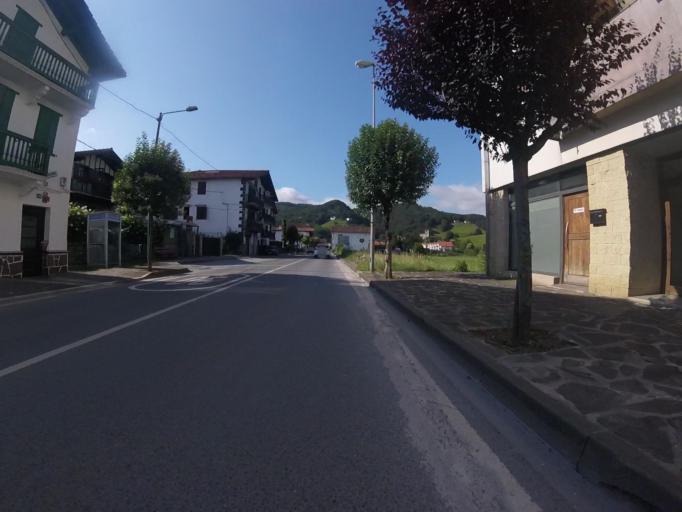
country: ES
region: Navarre
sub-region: Provincia de Navarra
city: Bera
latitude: 43.2758
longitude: -1.6884
